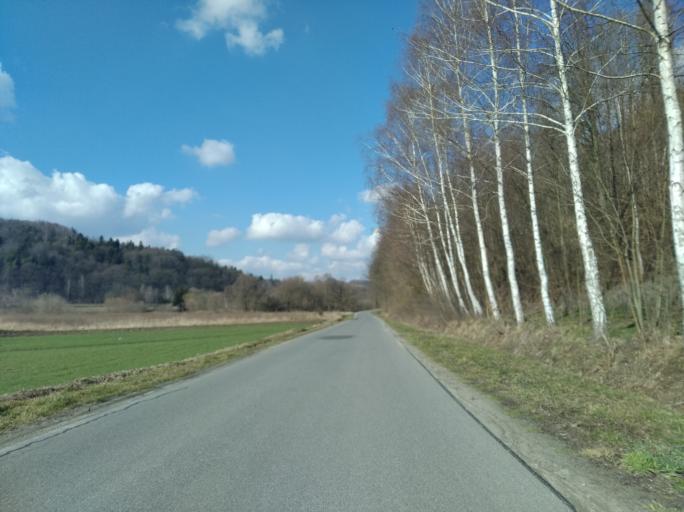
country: PL
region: Subcarpathian Voivodeship
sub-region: Powiat strzyzowski
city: Frysztak
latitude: 49.8500
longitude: 21.6246
